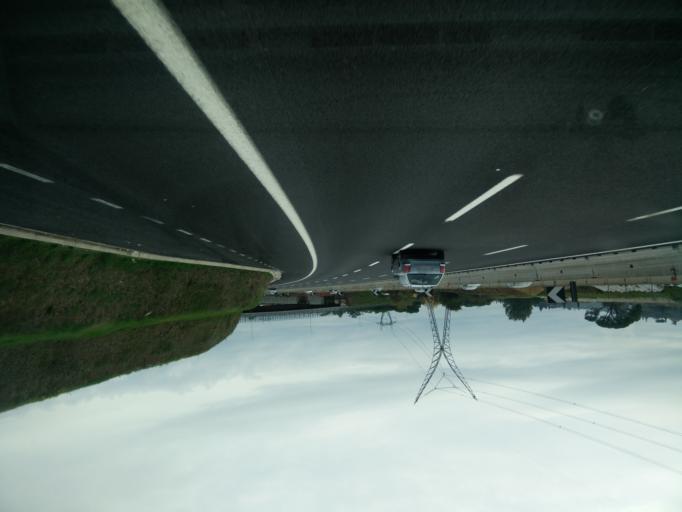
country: IT
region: Tuscany
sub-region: Province of Florence
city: Scandicci
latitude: 43.7453
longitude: 11.1751
